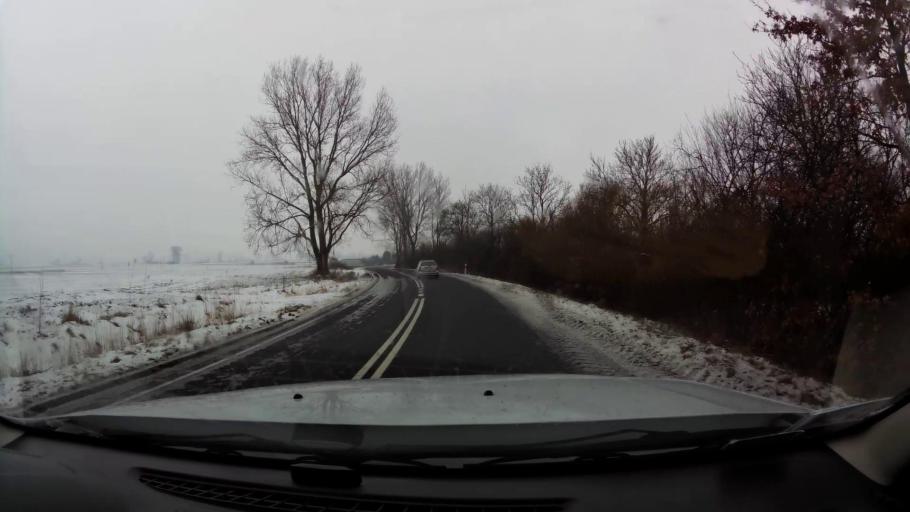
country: PL
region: West Pomeranian Voivodeship
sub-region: Powiat gryficki
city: Trzebiatow
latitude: 54.1030
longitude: 15.2659
